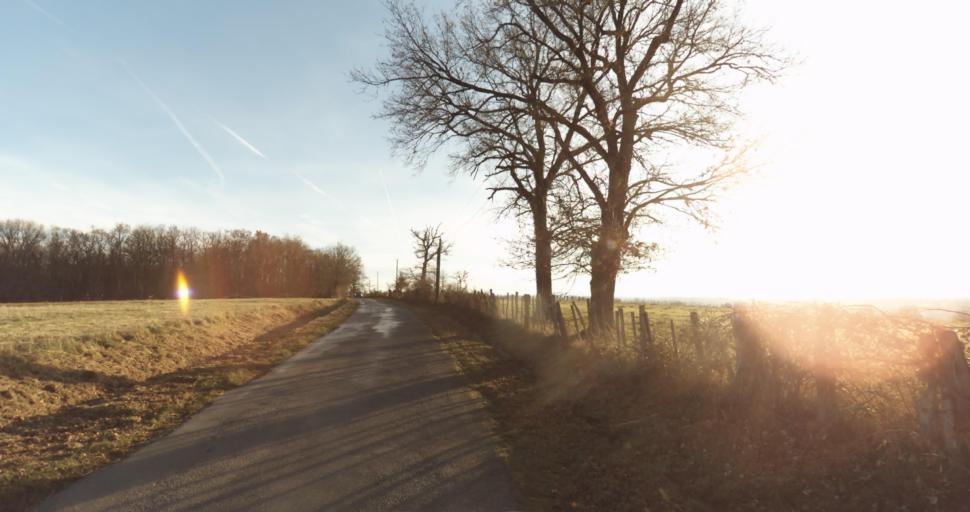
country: FR
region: Limousin
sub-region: Departement de la Haute-Vienne
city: Aixe-sur-Vienne
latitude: 45.7767
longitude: 1.1417
